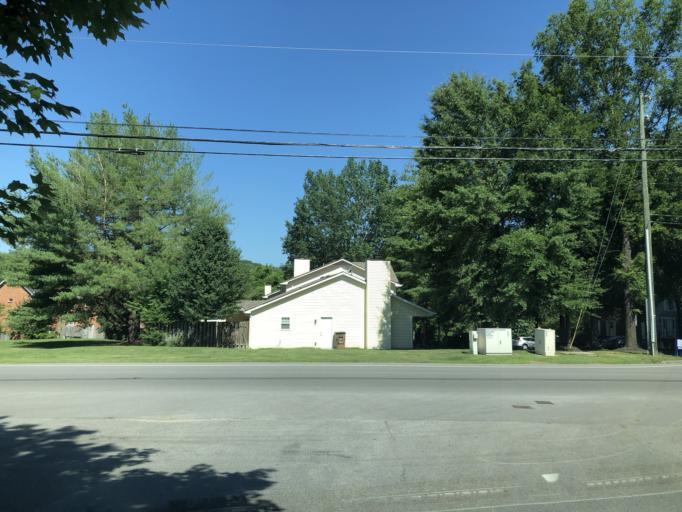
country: US
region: Tennessee
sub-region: Williamson County
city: Nolensville
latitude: 36.0427
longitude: -86.6705
